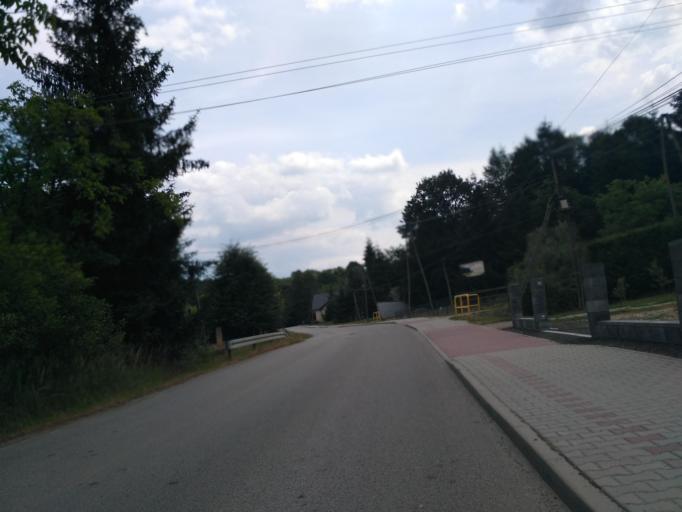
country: PL
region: Subcarpathian Voivodeship
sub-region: Powiat debicki
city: Brzeznica
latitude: 50.0428
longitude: 21.4918
